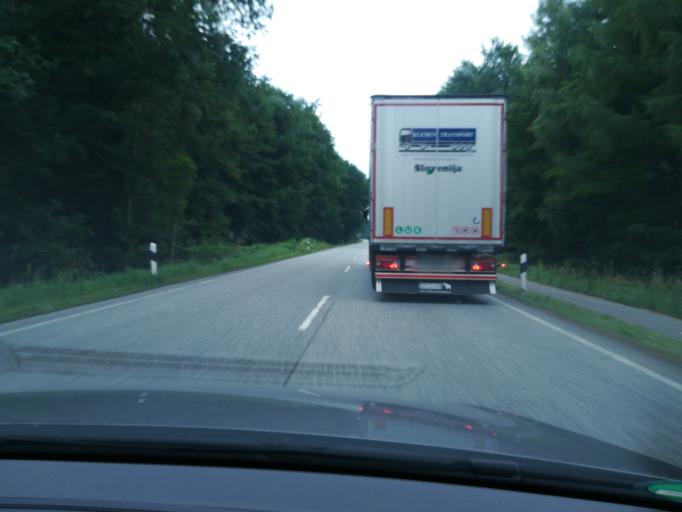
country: DE
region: Schleswig-Holstein
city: Brunstorf
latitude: 53.5329
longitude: 10.4318
